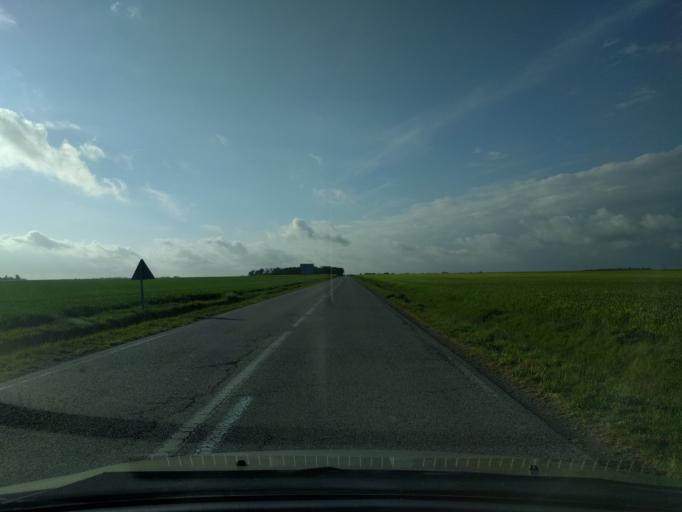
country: FR
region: Haute-Normandie
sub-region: Departement de l'Eure
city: Damville
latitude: 48.9082
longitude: 1.0218
